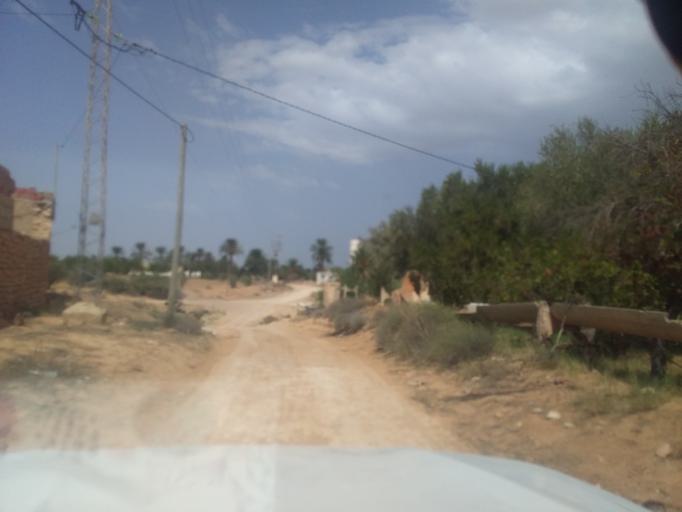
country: TN
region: Madanin
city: Medenine
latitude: 33.5954
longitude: 10.3249
